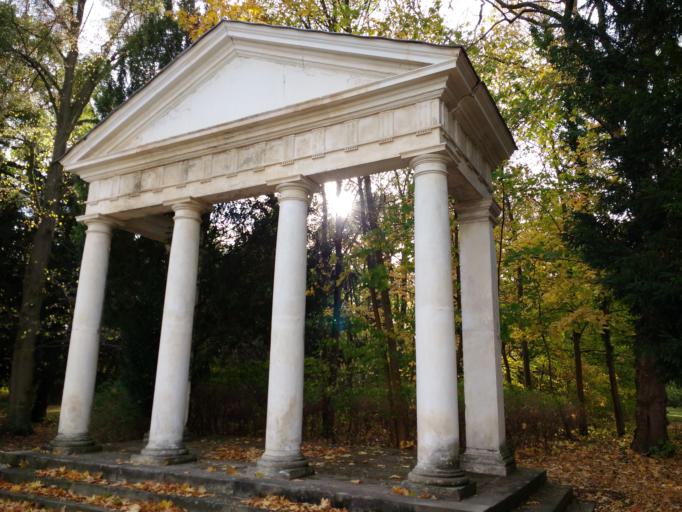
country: DE
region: Saxony-Anhalt
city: Dessau
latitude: 51.8441
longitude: 12.2298
